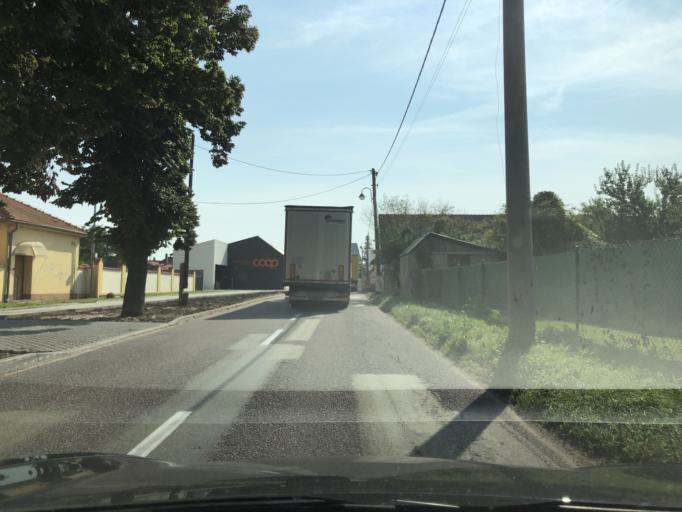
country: CZ
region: South Moravian
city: Brezi
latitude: 48.8210
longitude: 16.5642
